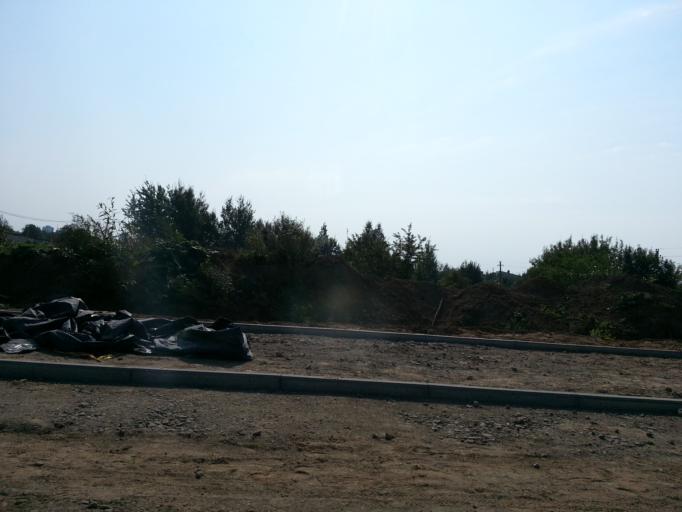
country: LT
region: Vilnius County
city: Pasilaiciai
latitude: 54.7356
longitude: 25.2069
